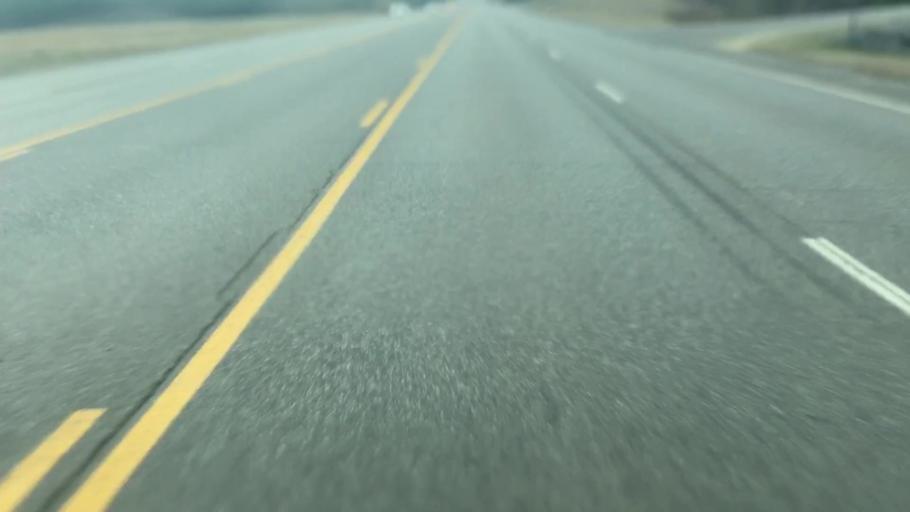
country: US
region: Alabama
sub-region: Walker County
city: Jasper
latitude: 33.8108
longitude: -87.2339
